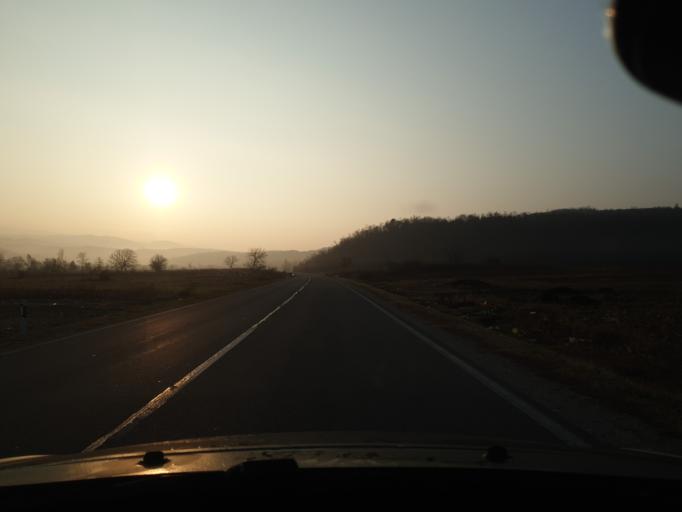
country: RS
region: Central Serbia
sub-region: Jablanicki Okrug
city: Leskovac
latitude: 42.9220
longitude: 22.0217
